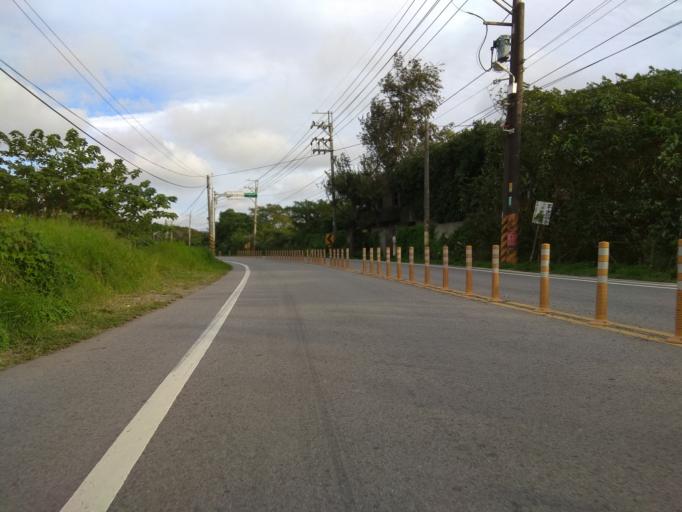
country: TW
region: Taiwan
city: Daxi
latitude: 24.9210
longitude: 121.1965
